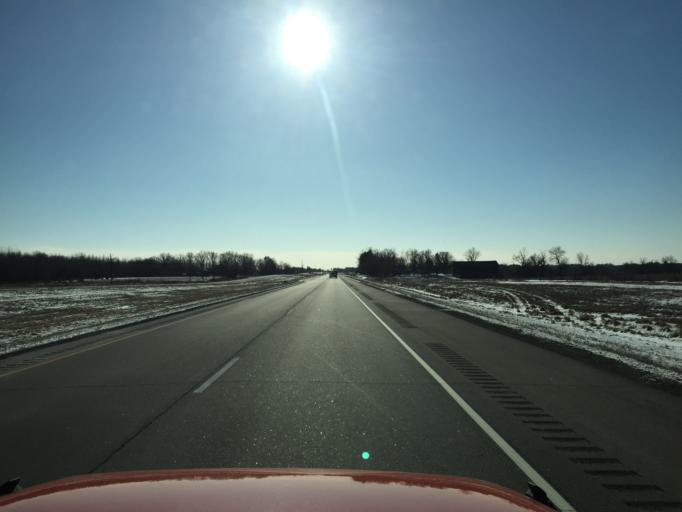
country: US
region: Minnesota
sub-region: Mille Lacs County
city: Milaca
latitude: 45.8054
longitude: -93.6550
